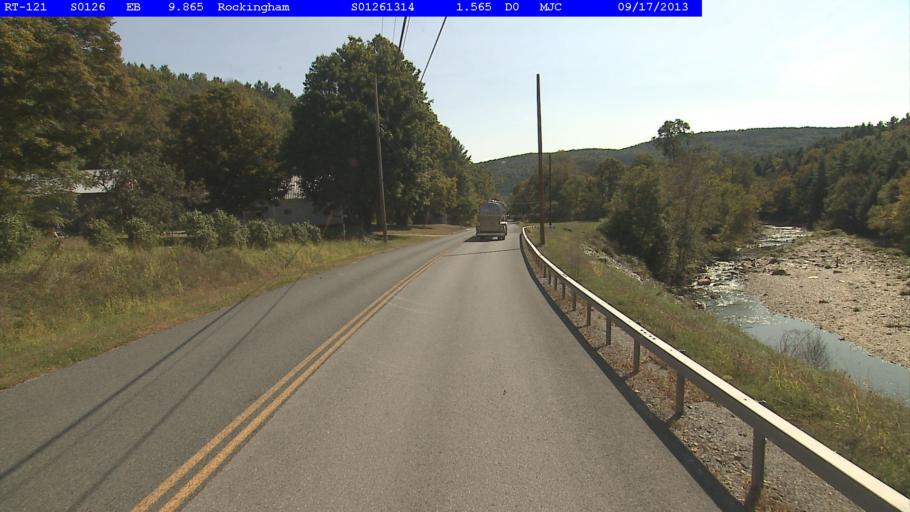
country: US
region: Vermont
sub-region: Windham County
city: Rockingham
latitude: 43.1395
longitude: -72.5328
